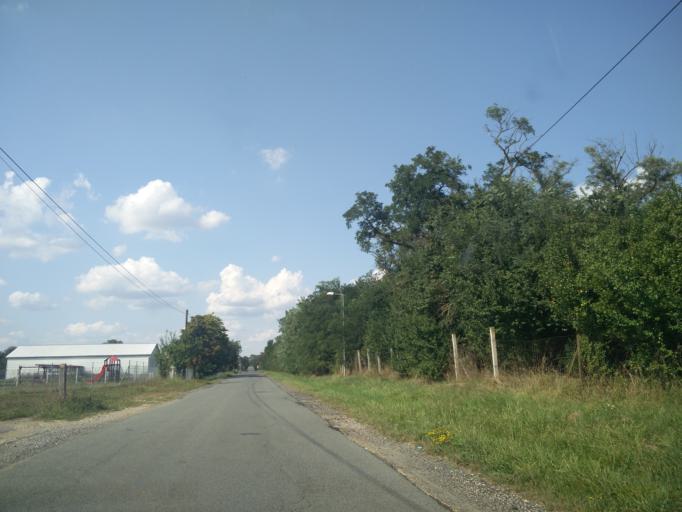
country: HU
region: Zala
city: Zalaegerszeg
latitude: 46.8838
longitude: 16.7935
